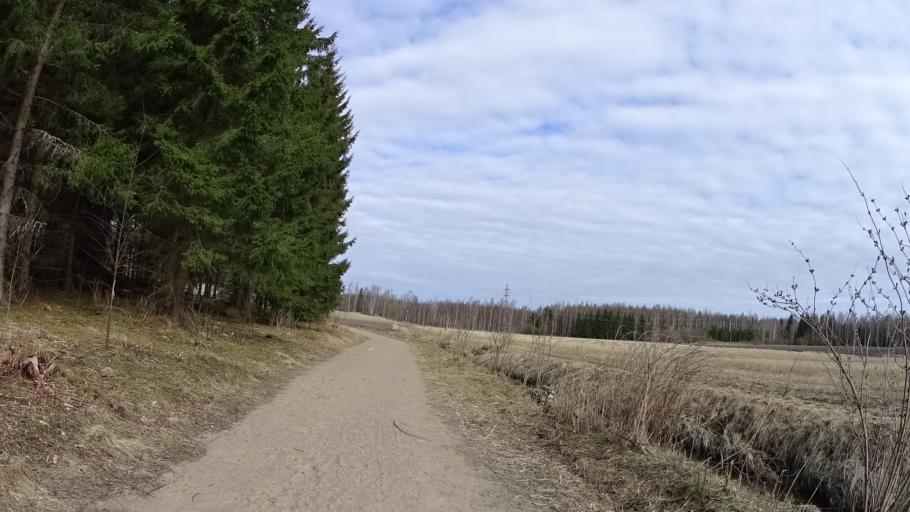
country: FI
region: Uusimaa
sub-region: Helsinki
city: Kilo
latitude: 60.2359
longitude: 24.7931
